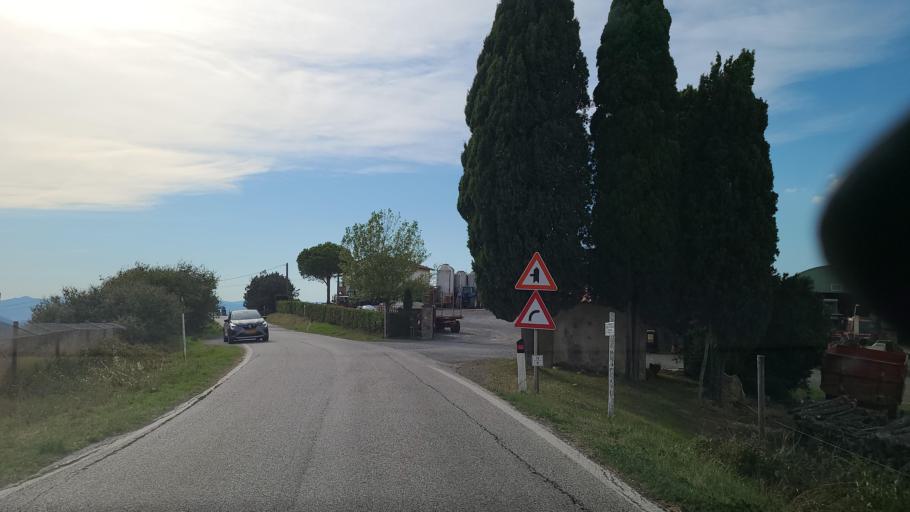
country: IT
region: Tuscany
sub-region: Provincia di Siena
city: San Gimignano
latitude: 43.4417
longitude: 10.9546
